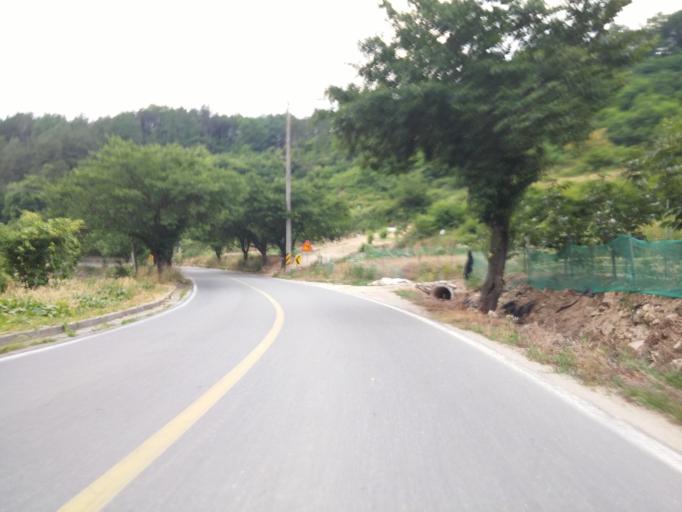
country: KR
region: Chungcheongnam-do
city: Kinzan
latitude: 36.1719
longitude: 127.5333
